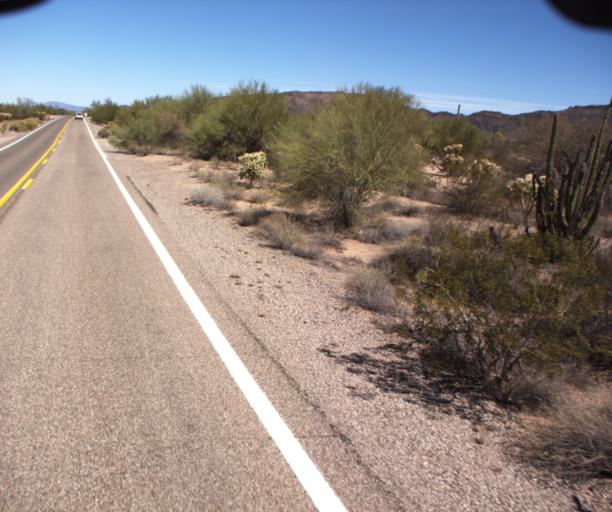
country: US
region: Arizona
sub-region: Pima County
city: Ajo
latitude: 32.1849
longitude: -112.7612
